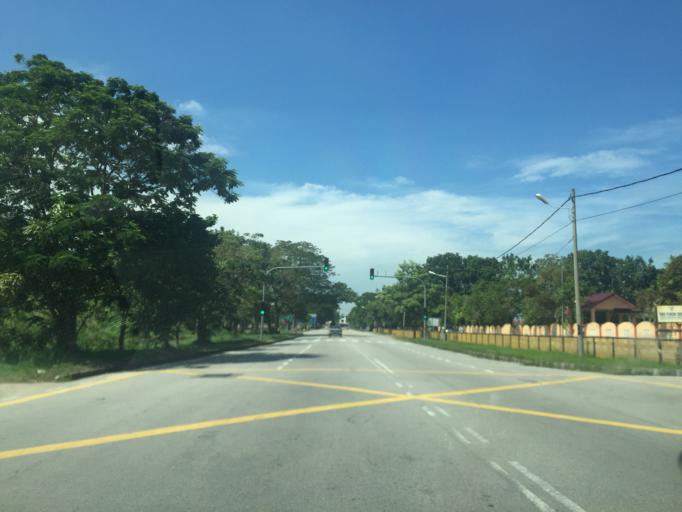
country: MY
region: Penang
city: Tasek Glugor
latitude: 5.4889
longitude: 100.4619
